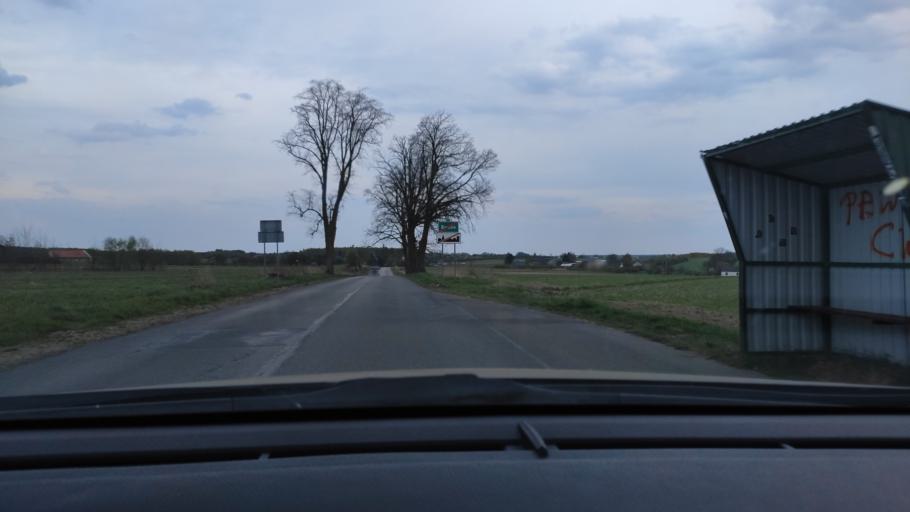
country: PL
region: Masovian Voivodeship
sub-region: Powiat kozienicki
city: Ryczywol
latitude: 51.5924
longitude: 21.3530
